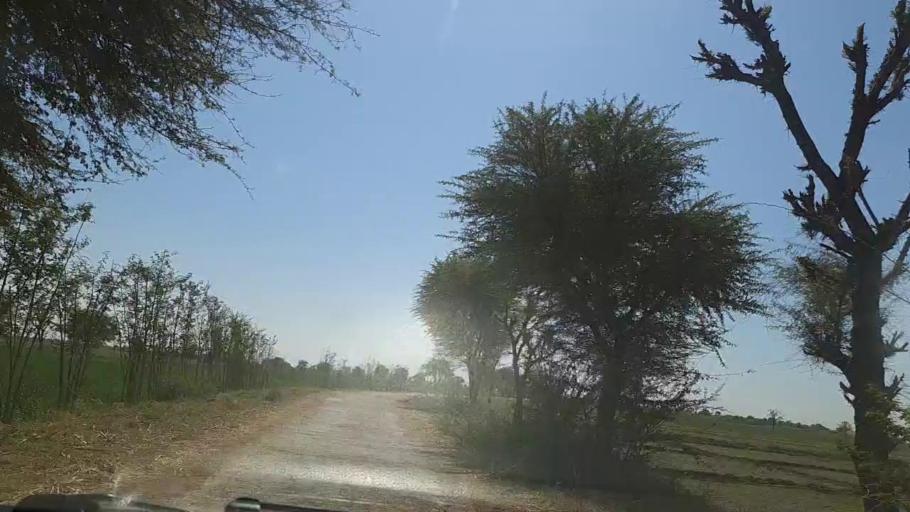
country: PK
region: Sindh
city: Dhoro Naro
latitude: 25.4889
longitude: 69.5439
